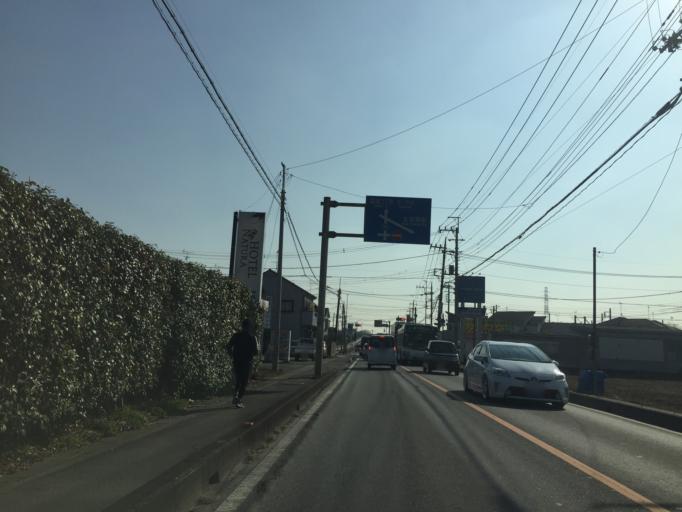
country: JP
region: Saitama
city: Shiki
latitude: 35.8353
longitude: 139.5988
